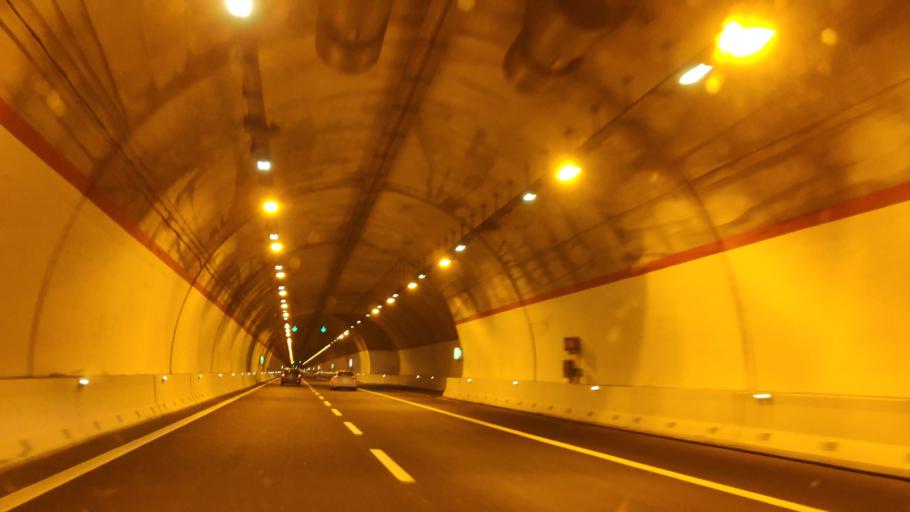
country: IT
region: Campania
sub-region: Provincia di Salerno
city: Casalbuono
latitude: 40.2028
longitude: 15.6847
